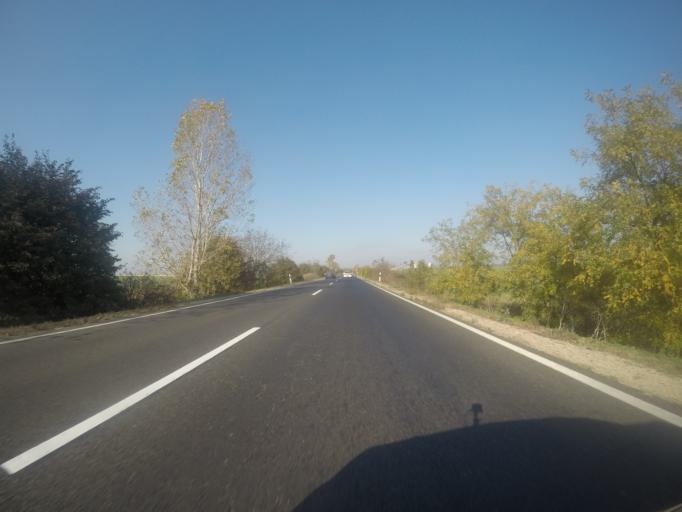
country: HU
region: Fejer
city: Baracs
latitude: 46.8841
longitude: 18.9189
